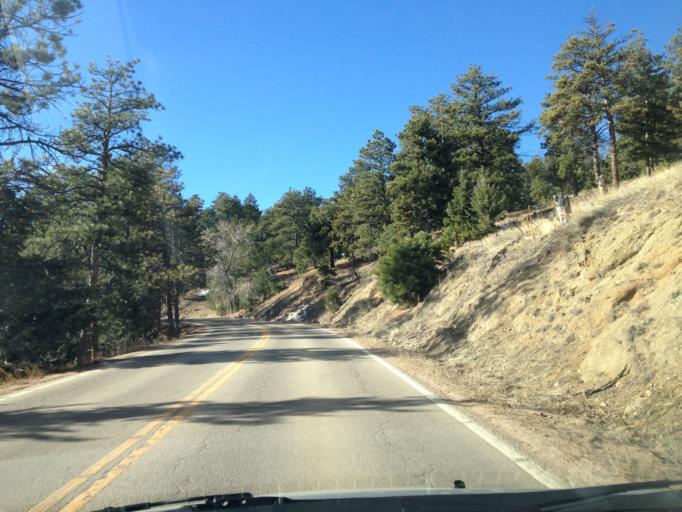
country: US
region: Colorado
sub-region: Boulder County
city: Boulder
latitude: 39.9924
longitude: -105.3138
